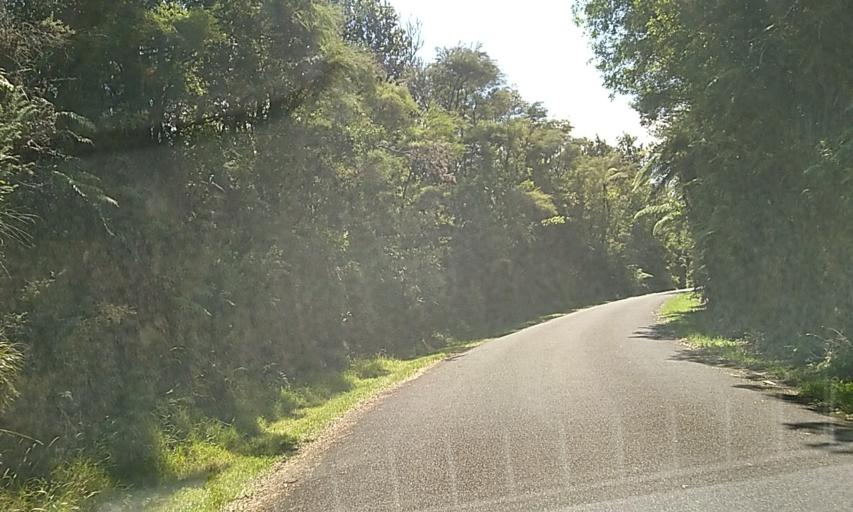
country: NZ
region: Bay of Plenty
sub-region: Tauranga City
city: Tauranga
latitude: -37.8202
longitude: 176.0414
